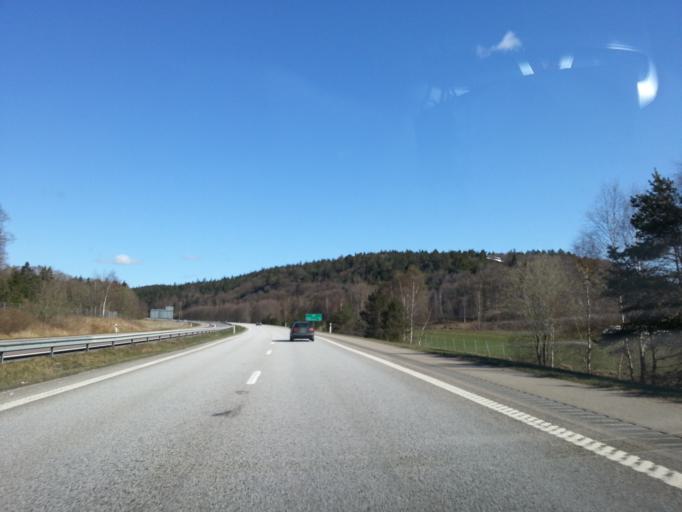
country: SE
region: Vaestra Goetaland
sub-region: Stenungsunds Kommun
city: Stenungsund
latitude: 58.0671
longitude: 11.8902
